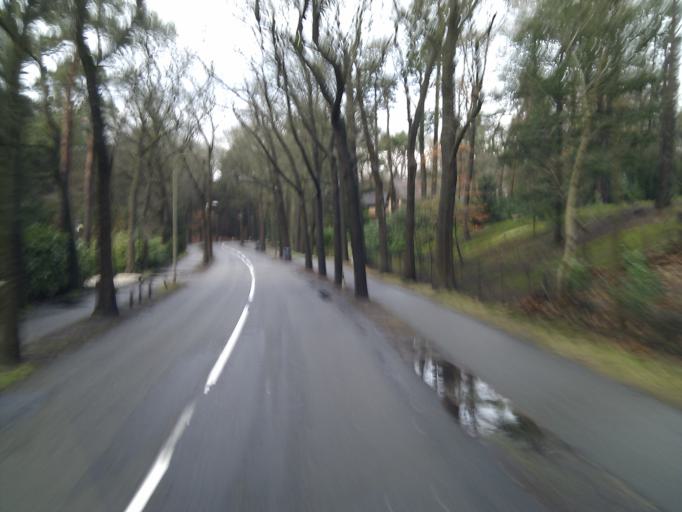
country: NL
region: Utrecht
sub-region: Gemeente Zeist
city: Zeist
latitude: 52.1171
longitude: 5.2385
